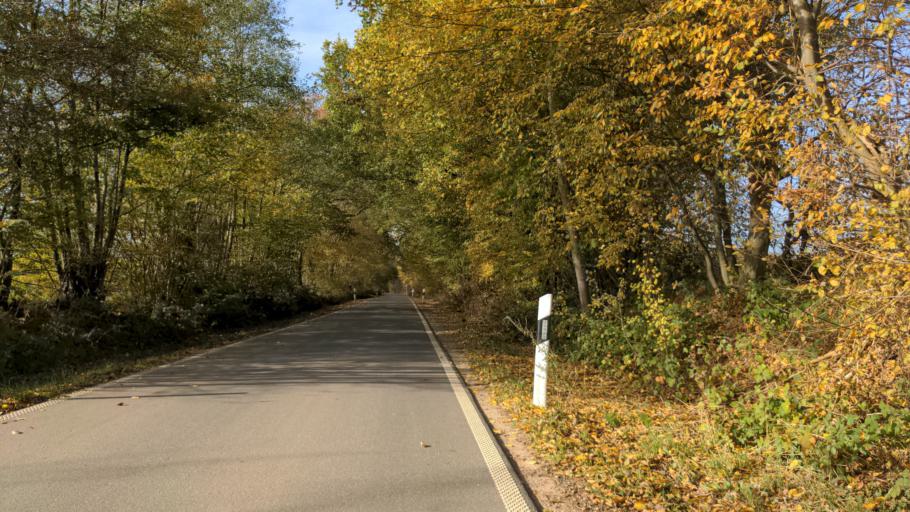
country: DE
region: Schleswig-Holstein
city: Hamberge
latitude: 53.8244
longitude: 10.5803
